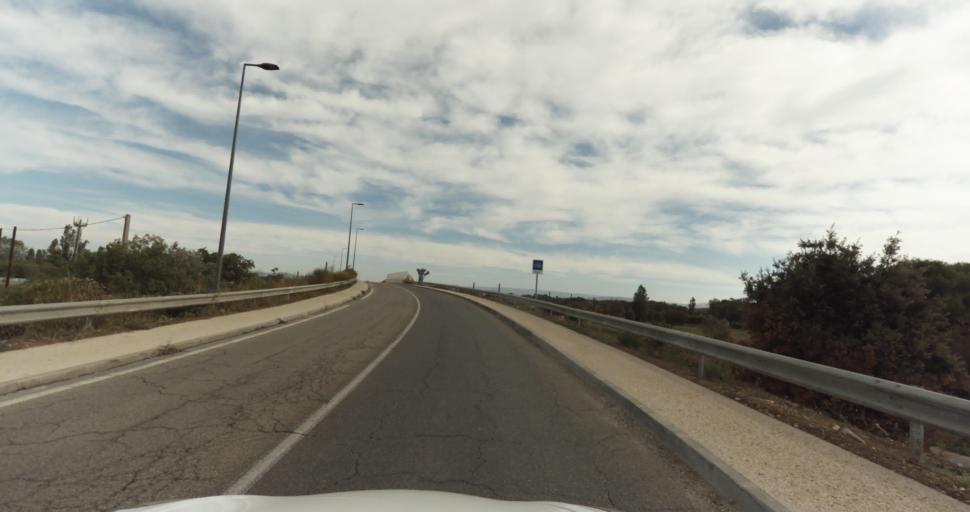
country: FR
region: Provence-Alpes-Cote d'Azur
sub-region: Departement des Bouches-du-Rhone
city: Miramas
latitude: 43.6036
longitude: 5.0082
